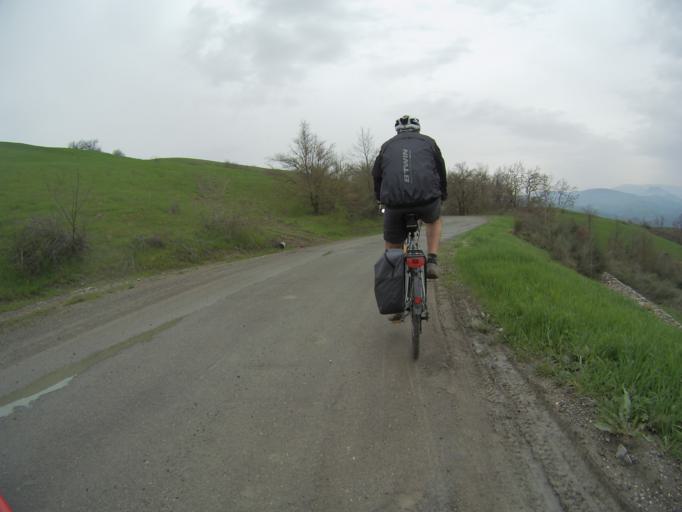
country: IT
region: Emilia-Romagna
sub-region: Provincia di Reggio Emilia
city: Ciano d'Enza
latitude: 44.5414
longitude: 10.4412
